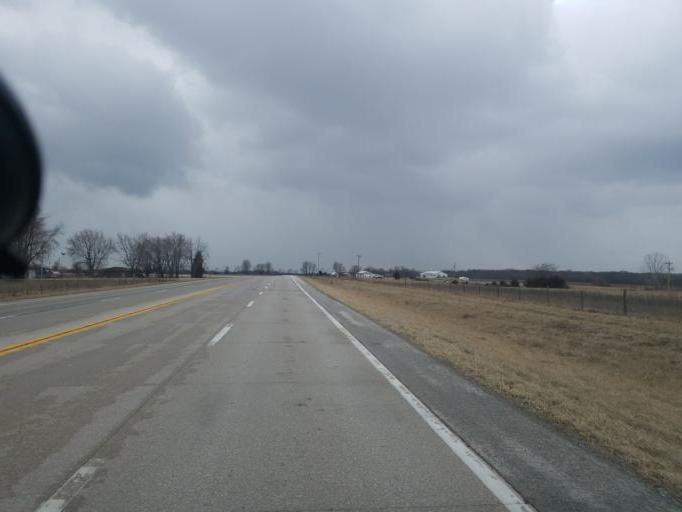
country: US
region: Missouri
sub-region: Macon County
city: Macon
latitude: 39.7899
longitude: -92.4804
